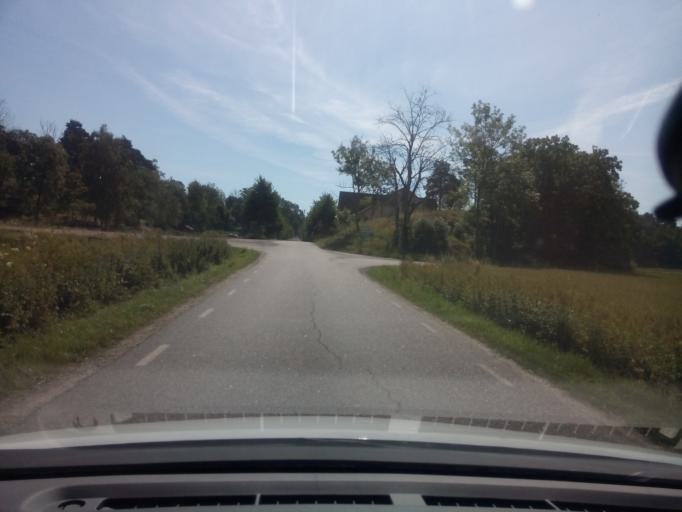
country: SE
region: Soedermanland
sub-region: Trosa Kommun
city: Trosa
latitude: 58.8103
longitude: 17.3614
